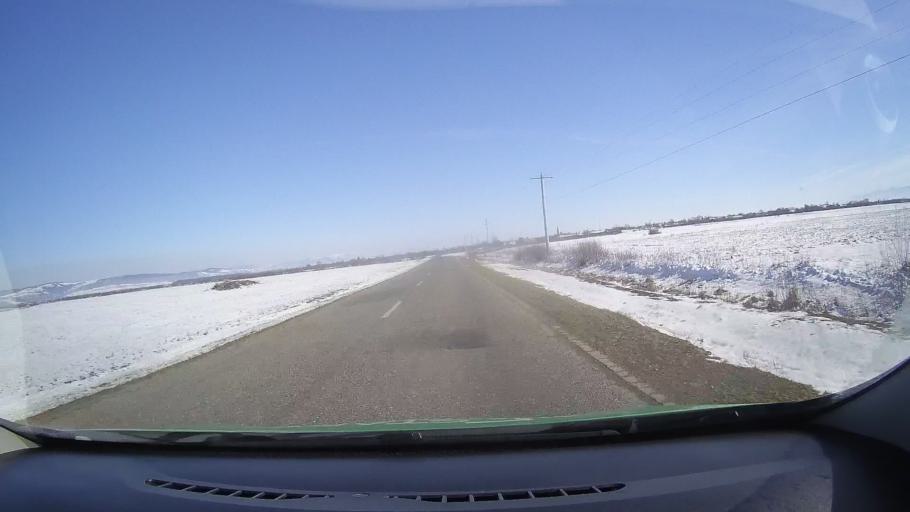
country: RO
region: Brasov
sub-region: Comuna Dragus
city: Dragus
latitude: 45.7567
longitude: 24.7613
